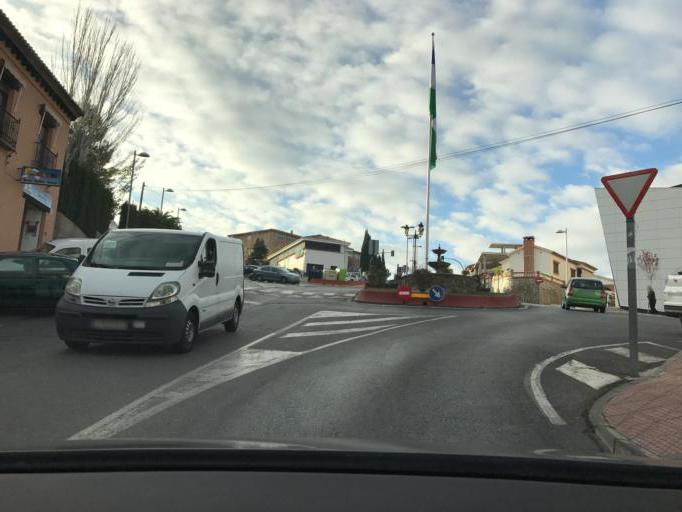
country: ES
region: Andalusia
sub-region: Provincia de Granada
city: Cajar
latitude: 37.1338
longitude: -3.5582
